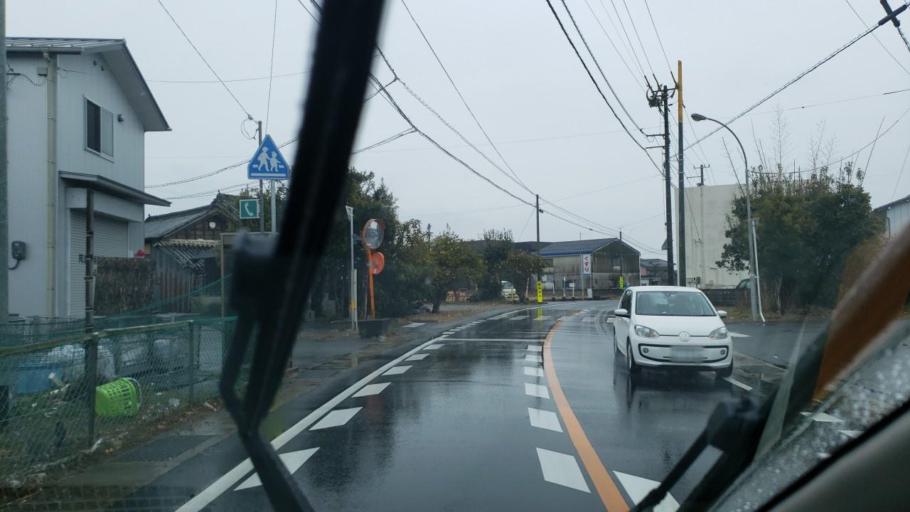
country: JP
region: Tokushima
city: Kamojimacho-jogejima
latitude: 34.0994
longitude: 134.3760
